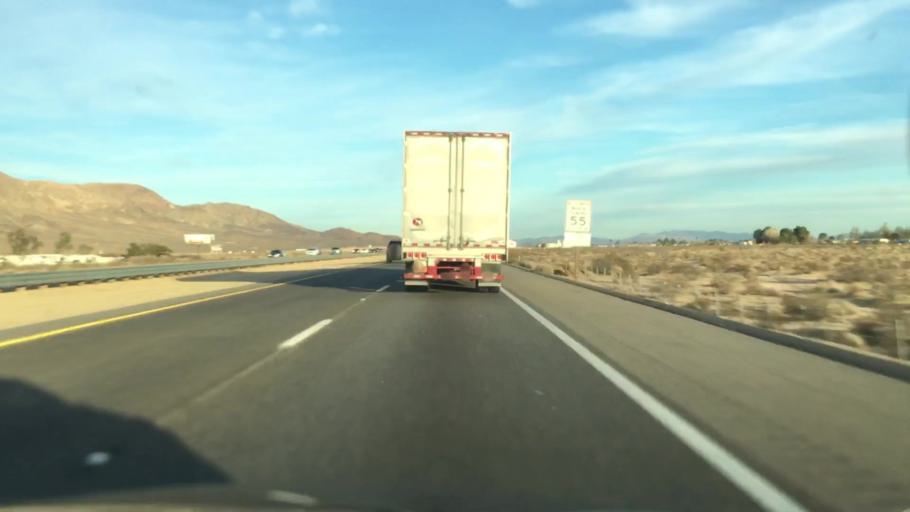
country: US
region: California
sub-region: San Bernardino County
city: Barstow
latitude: 34.9072
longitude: -116.8522
